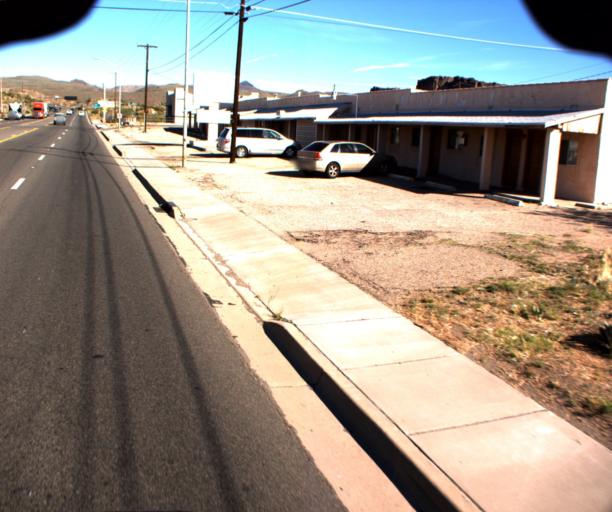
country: US
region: Arizona
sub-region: Mohave County
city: Kingman
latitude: 35.1964
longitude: -114.0753
